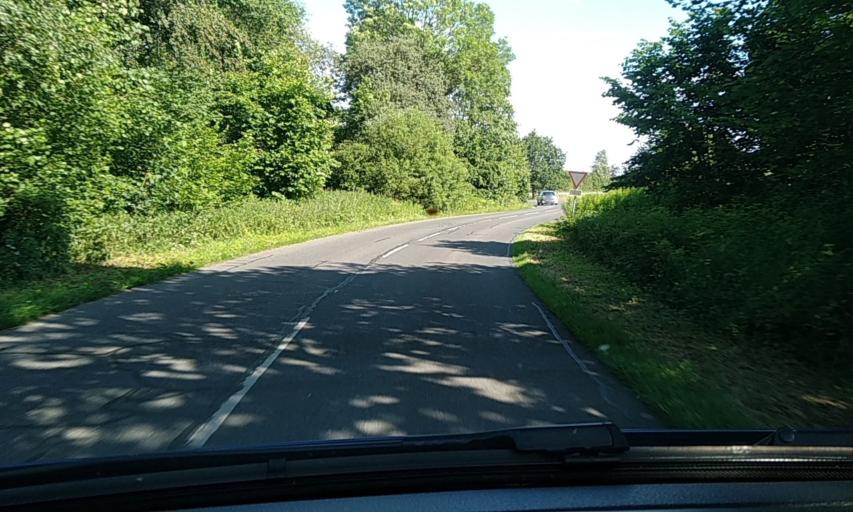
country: DE
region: Schleswig-Holstein
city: Fockbek
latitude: 54.2786
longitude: 9.5740
